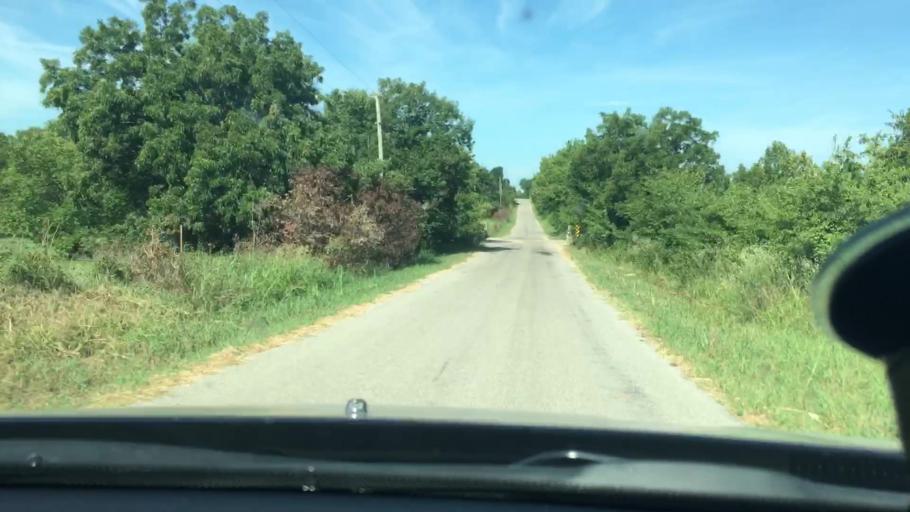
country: US
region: Oklahoma
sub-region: Carter County
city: Lone Grove
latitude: 34.2674
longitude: -97.2579
